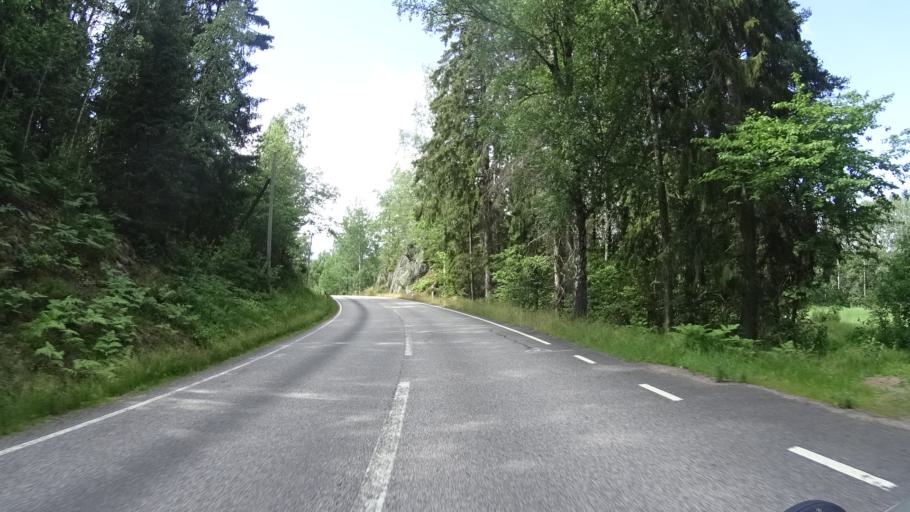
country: SE
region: Kalmar
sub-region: Vasterviks Kommun
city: Overum
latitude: 58.0311
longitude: 16.2369
